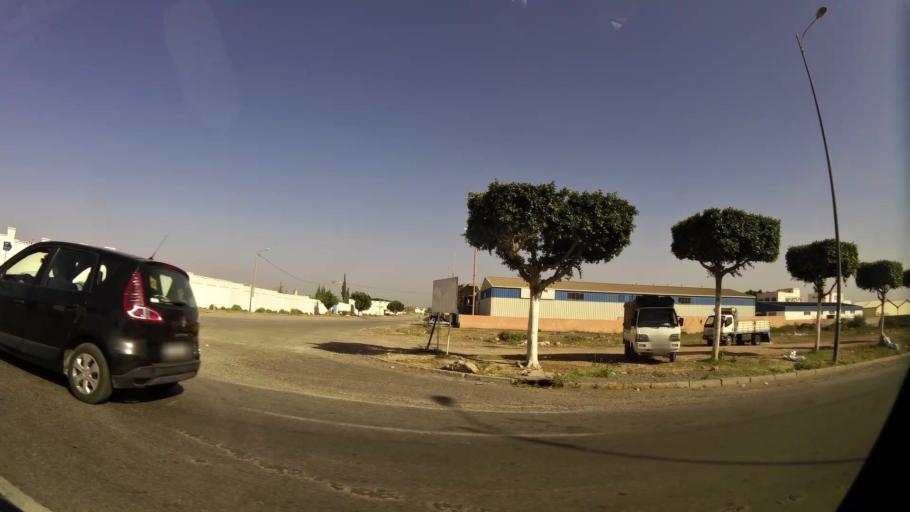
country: MA
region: Souss-Massa-Draa
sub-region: Inezgane-Ait Mellou
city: Inezgane
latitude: 30.3869
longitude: -9.5149
